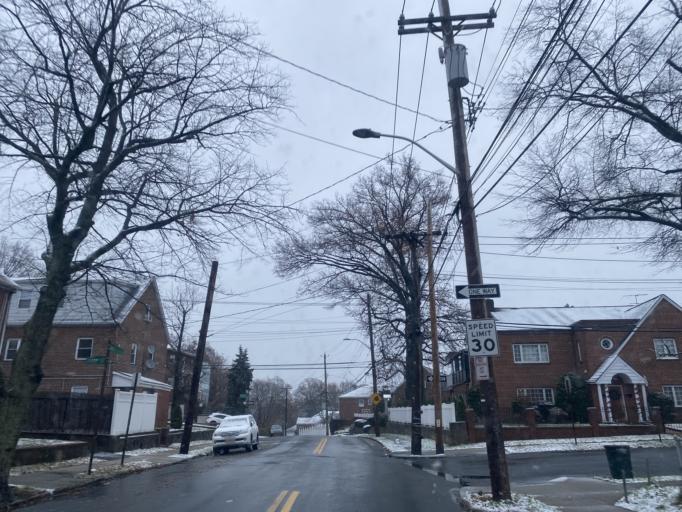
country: US
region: New York
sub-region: Westchester County
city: Mount Vernon
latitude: 40.9062
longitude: -73.8611
